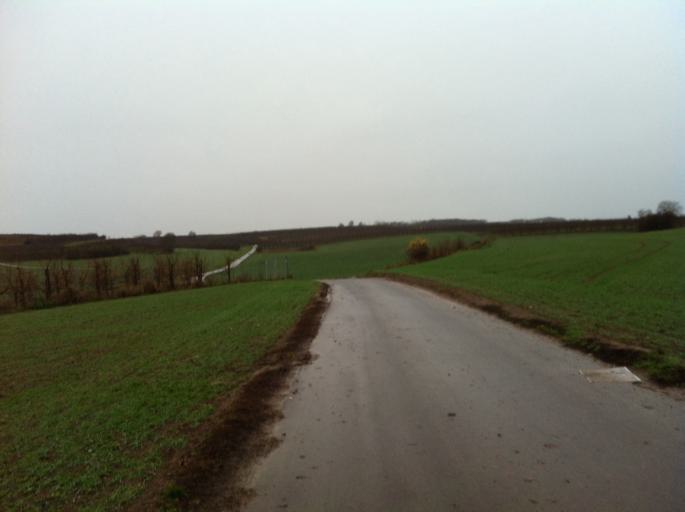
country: DE
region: Rheinland-Pfalz
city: Budenheim
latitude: 49.9804
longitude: 8.1644
